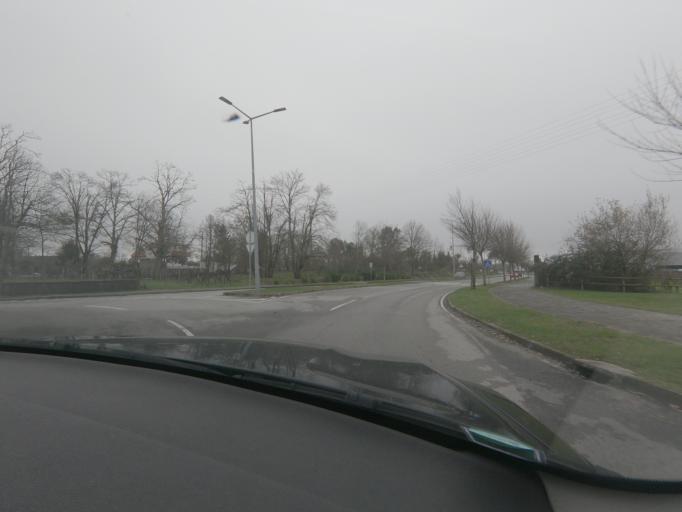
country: PT
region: Viseu
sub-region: Concelho de Tondela
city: Tondela
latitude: 40.5307
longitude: -8.0868
